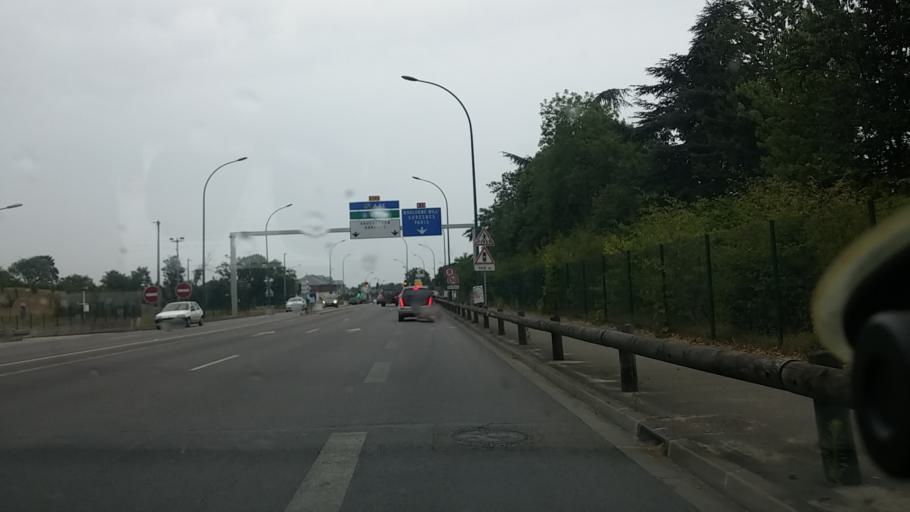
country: FR
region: Ile-de-France
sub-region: Departement des Hauts-de-Seine
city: Vaucresson
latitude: 48.8307
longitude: 2.1523
